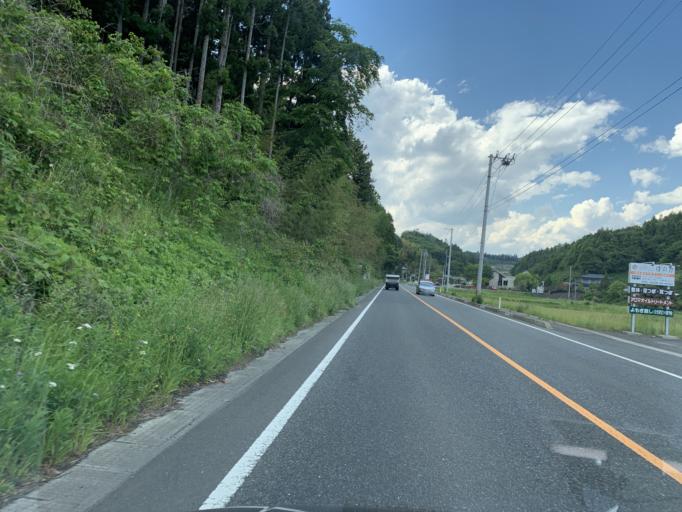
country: JP
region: Miyagi
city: Wakuya
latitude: 38.5549
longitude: 141.1377
